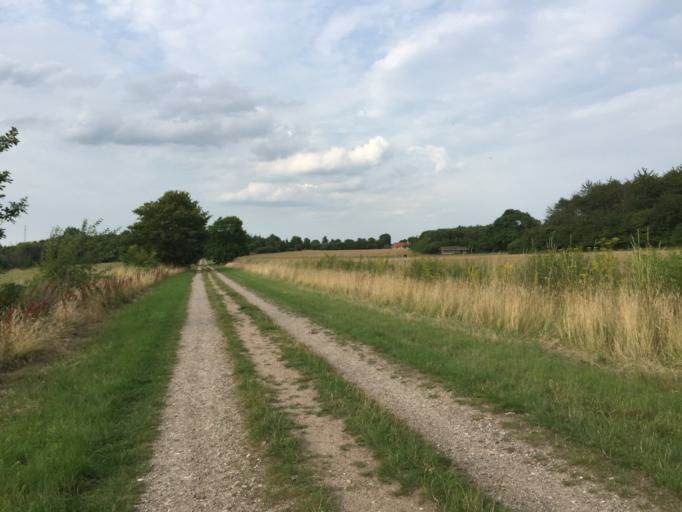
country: DK
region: South Denmark
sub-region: Odense Kommune
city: Neder Holluf
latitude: 55.3815
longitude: 10.4640
